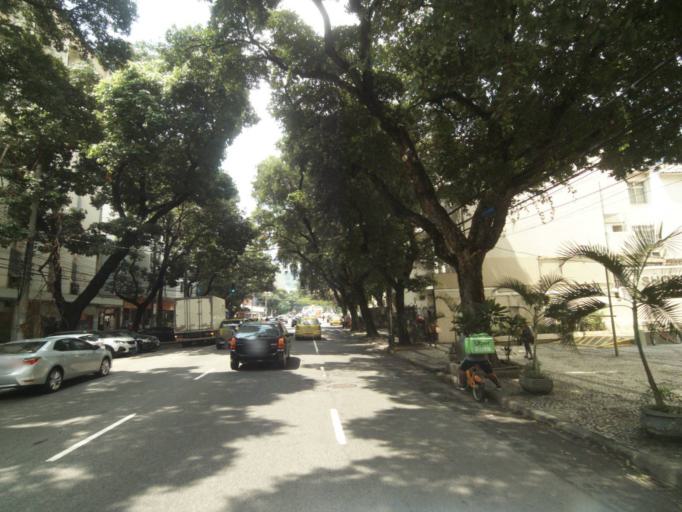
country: BR
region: Rio de Janeiro
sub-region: Rio De Janeiro
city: Rio de Janeiro
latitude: -22.9239
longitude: -43.2289
